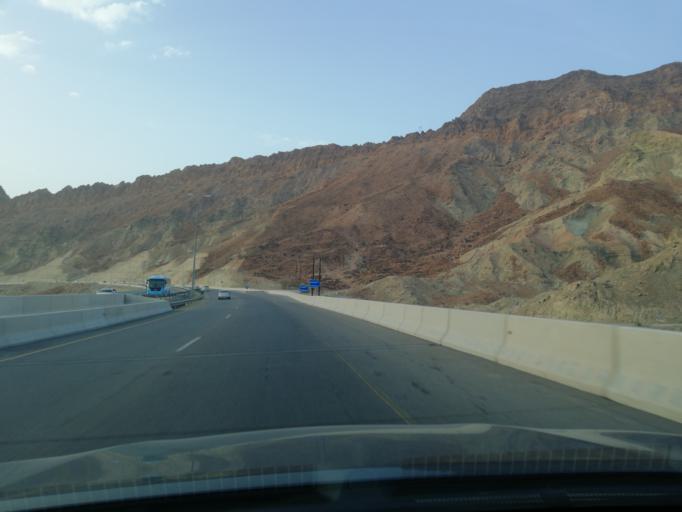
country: OM
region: Muhafazat ad Dakhiliyah
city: Bidbid
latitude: 23.4468
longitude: 58.1231
